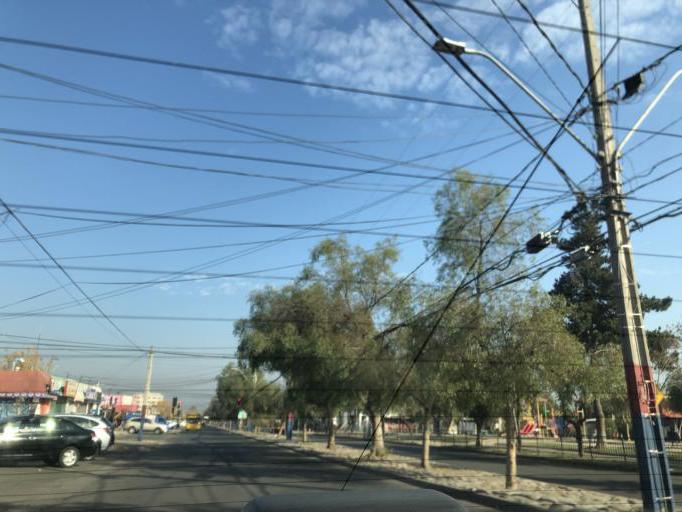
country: CL
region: Santiago Metropolitan
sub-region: Provincia de Cordillera
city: Puente Alto
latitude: -33.5937
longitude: -70.5723
